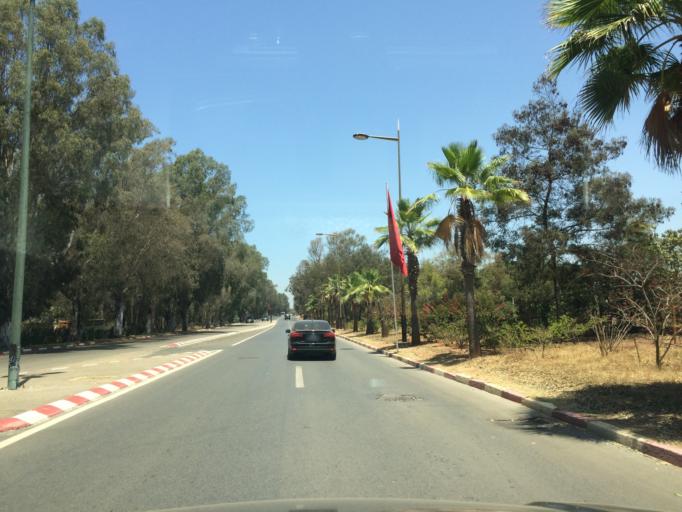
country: MA
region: Rabat-Sale-Zemmour-Zaer
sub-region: Skhirate-Temara
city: Temara
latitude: 33.9285
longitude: -6.8213
